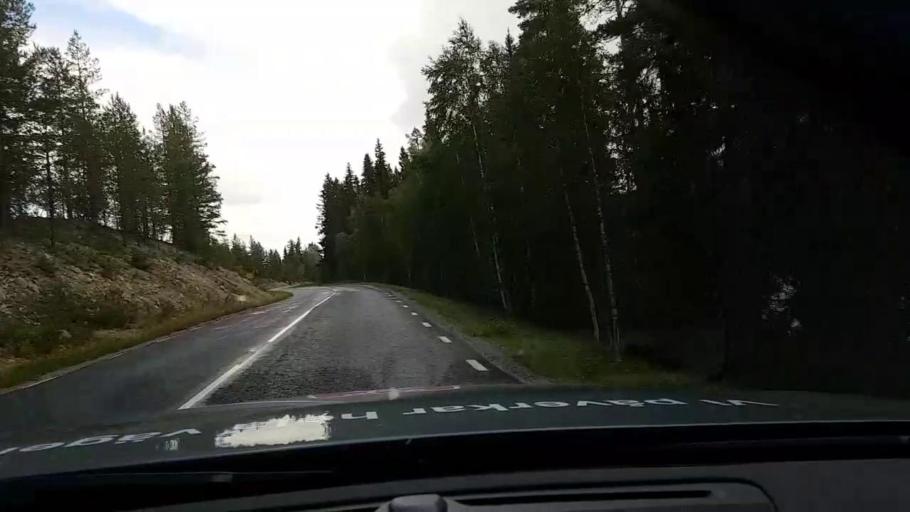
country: SE
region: Vaesterbotten
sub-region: Asele Kommun
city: Asele
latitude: 63.8345
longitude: 17.4449
